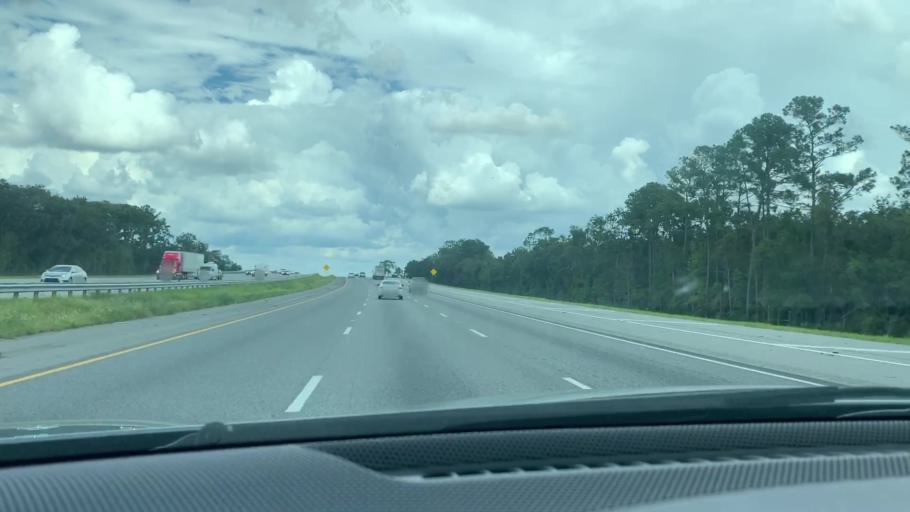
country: US
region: Georgia
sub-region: Glynn County
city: Dock Junction
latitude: 31.1621
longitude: -81.5567
